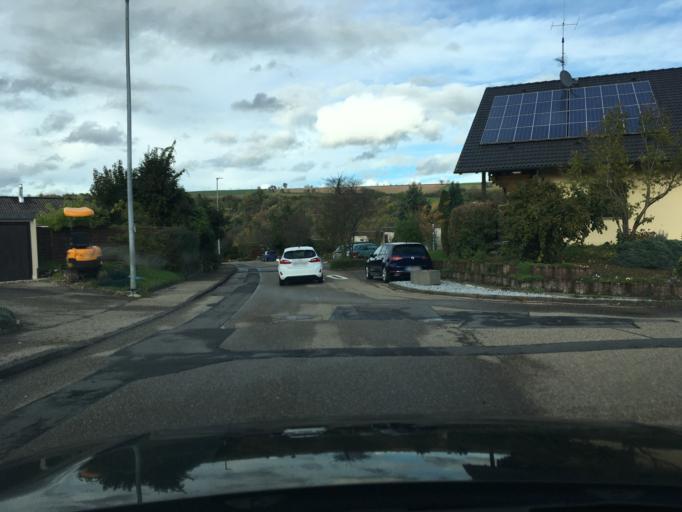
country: DE
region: Baden-Wuerttemberg
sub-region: Regierungsbezirk Stuttgart
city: Mockmuhl
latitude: 49.3190
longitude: 9.3730
